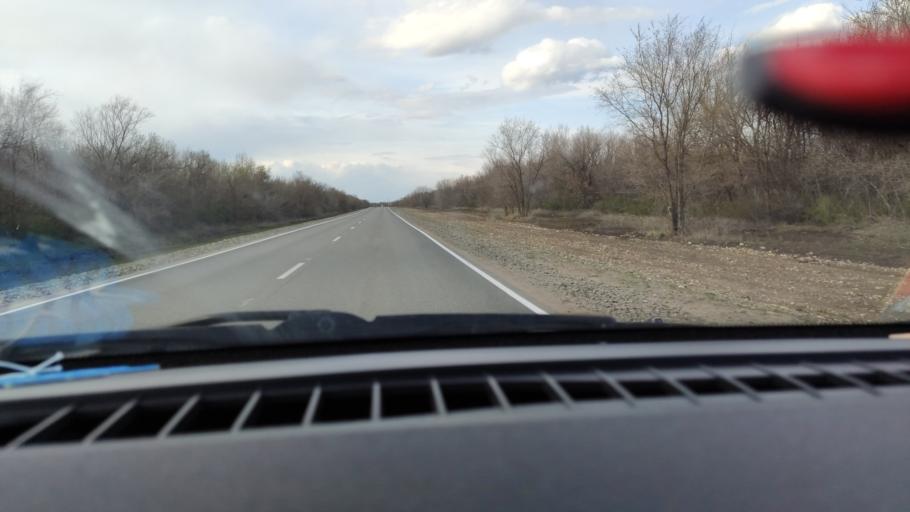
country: RU
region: Saratov
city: Privolzhskiy
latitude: 51.1491
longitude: 45.9623
